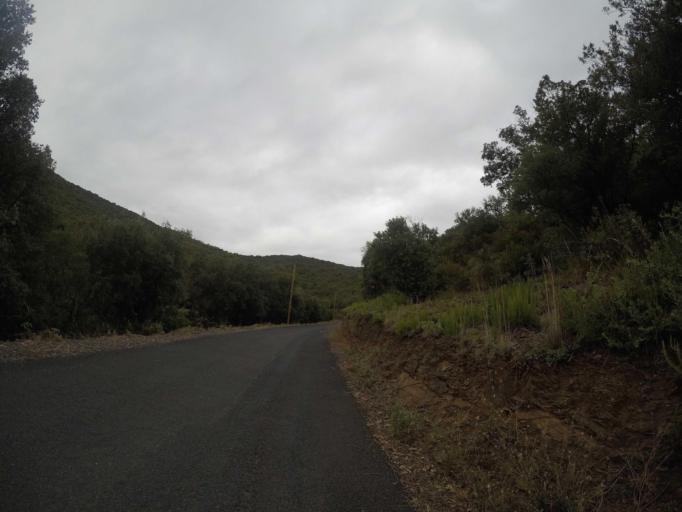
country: FR
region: Languedoc-Roussillon
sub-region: Departement des Pyrenees-Orientales
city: Ille-sur-Tet
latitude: 42.6304
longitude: 2.6134
